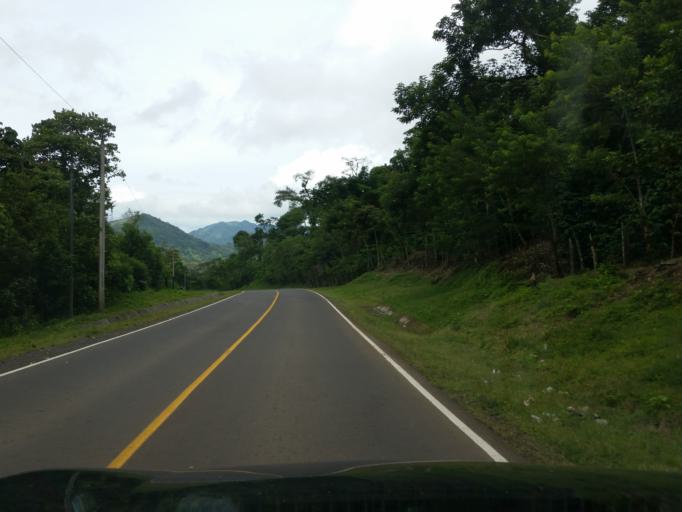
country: NI
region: Matagalpa
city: San Ramon
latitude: 12.9596
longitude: -85.8586
